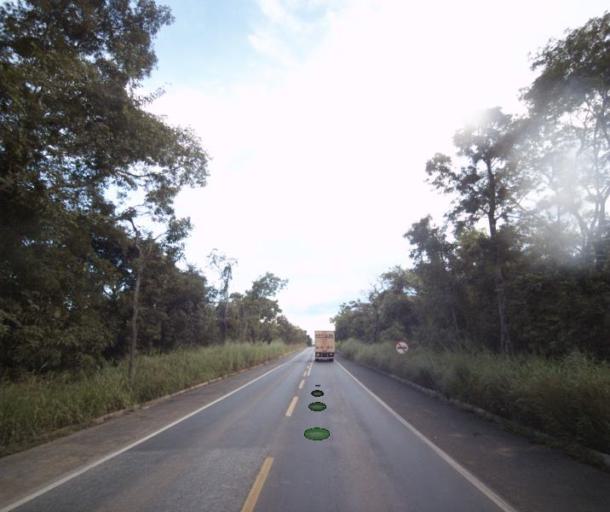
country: BR
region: Goias
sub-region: Uruacu
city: Uruacu
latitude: -14.1264
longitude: -49.1096
